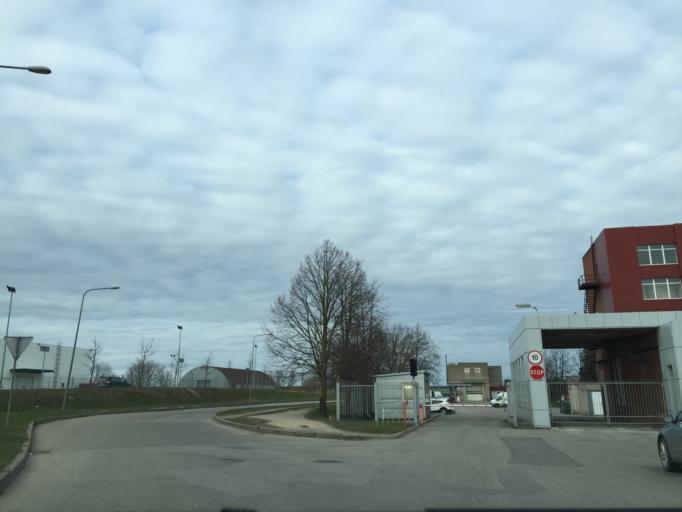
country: LT
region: Klaipedos apskritis
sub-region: Klaipeda
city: Klaipeda
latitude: 55.6956
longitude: 21.1743
